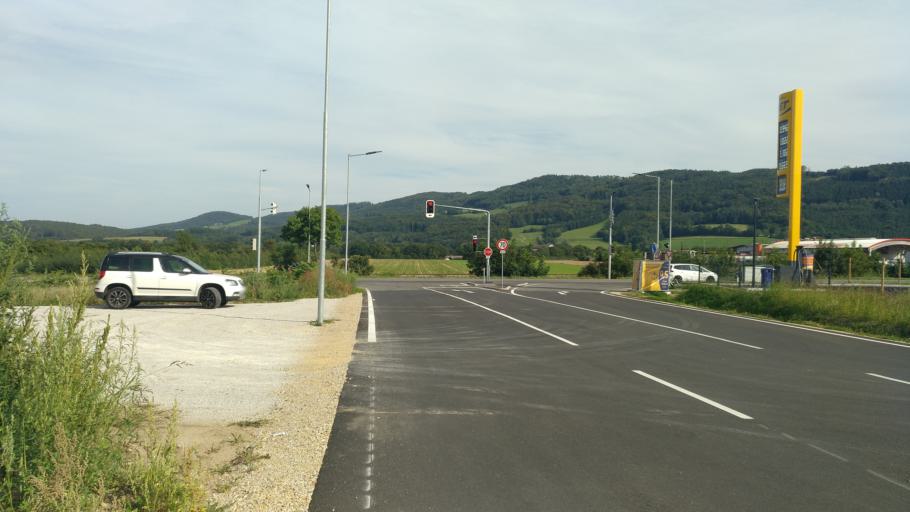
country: AT
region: Lower Austria
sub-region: Politischer Bezirk Sankt Polten
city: Wilhelmsburg
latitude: 48.1186
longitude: 15.6085
